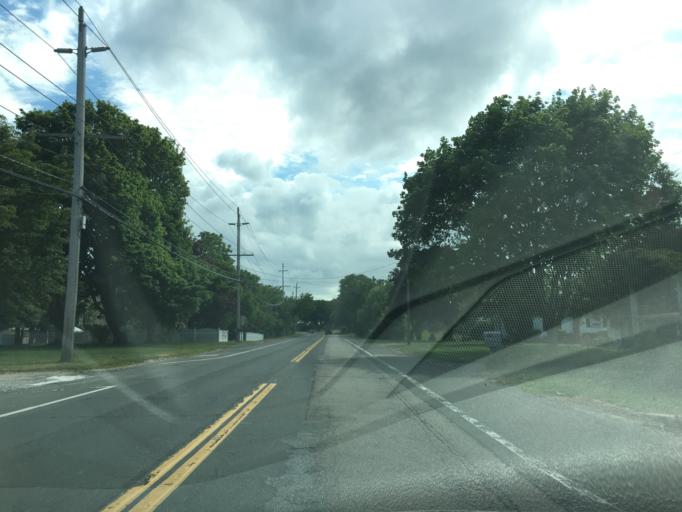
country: US
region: New York
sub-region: Suffolk County
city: Southold
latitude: 41.0832
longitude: -72.4201
